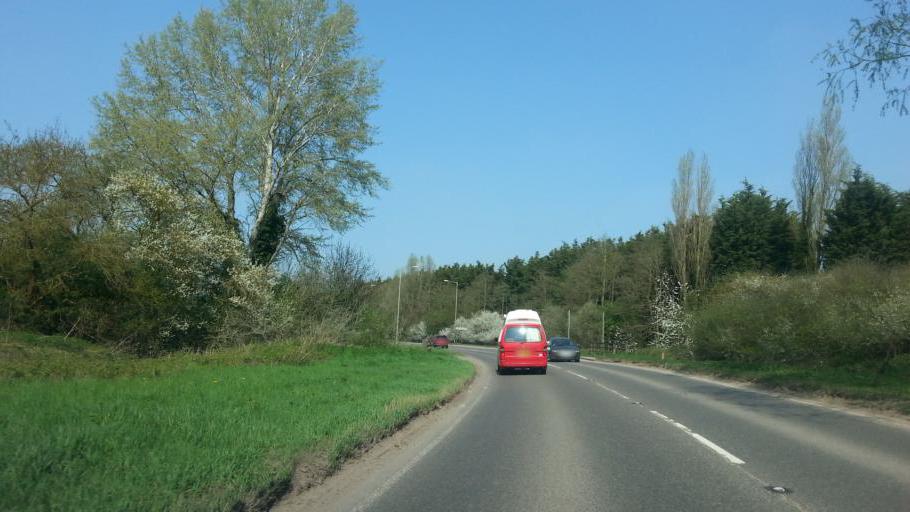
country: GB
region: England
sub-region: Cambridgeshire
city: Hemingford Grey
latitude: 52.3079
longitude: -0.0868
